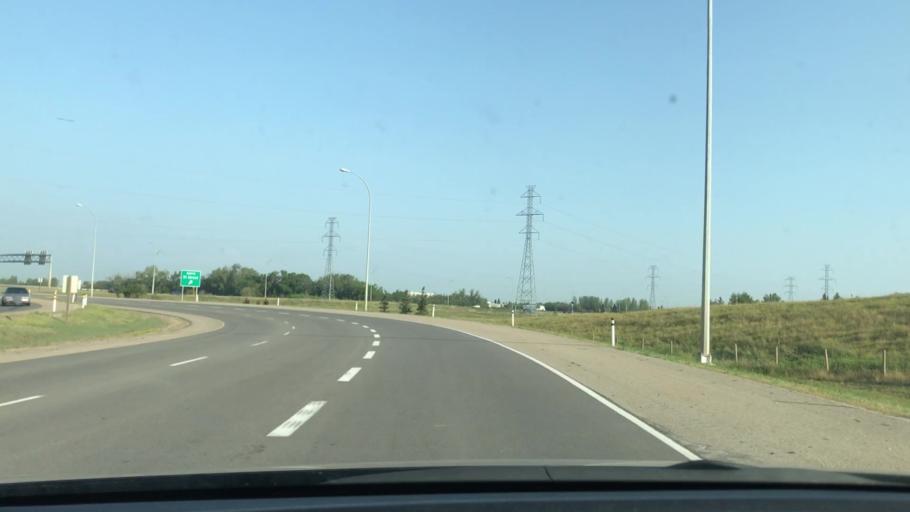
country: CA
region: Alberta
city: Beaumont
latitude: 53.4392
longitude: -113.4634
